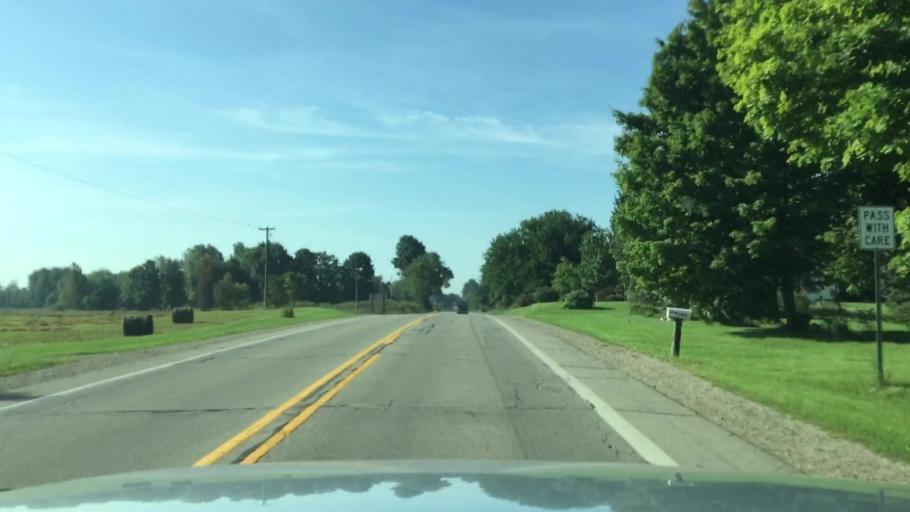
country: US
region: Michigan
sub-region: Lenawee County
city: Hudson
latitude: 41.9415
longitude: -84.3671
